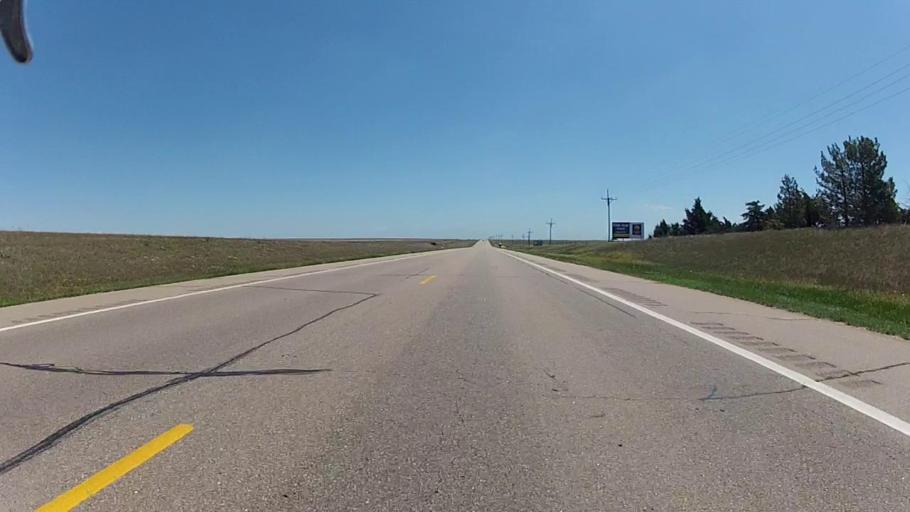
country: US
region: Kansas
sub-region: Ford County
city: Dodge City
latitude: 37.7092
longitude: -100.1224
